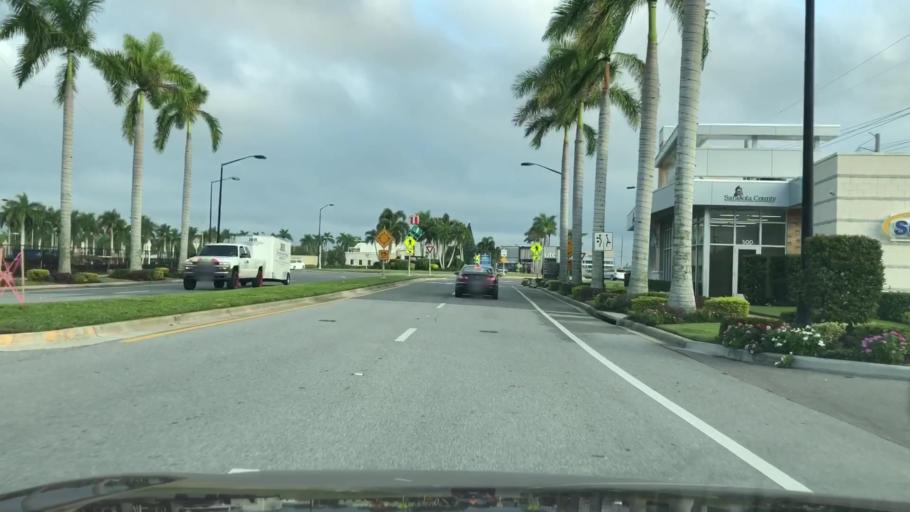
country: US
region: Florida
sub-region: Sarasota County
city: The Meadows
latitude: 27.3804
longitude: -82.4556
